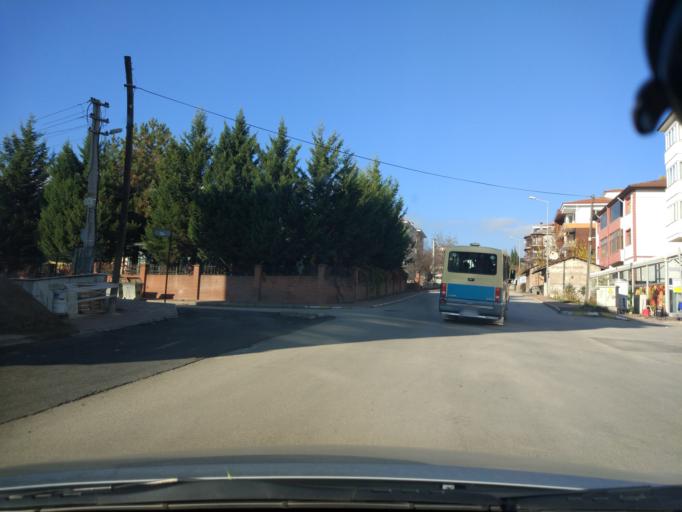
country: TR
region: Karabuk
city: Safranbolu
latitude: 41.2477
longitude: 32.6746
